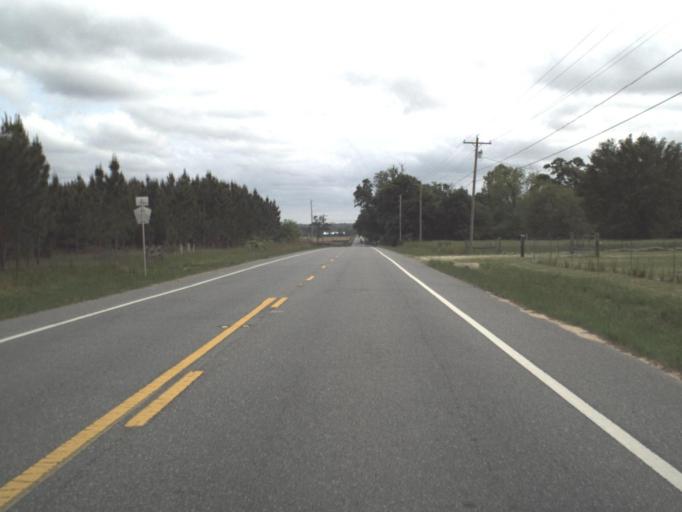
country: US
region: Florida
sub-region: Santa Rosa County
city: Point Baker
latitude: 30.8330
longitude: -87.0488
